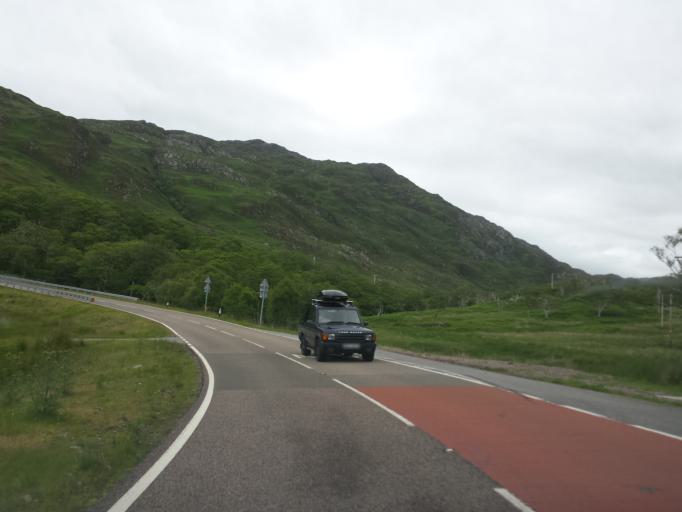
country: GB
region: Scotland
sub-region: Argyll and Bute
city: Isle Of Mull
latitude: 56.9001
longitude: -5.7533
